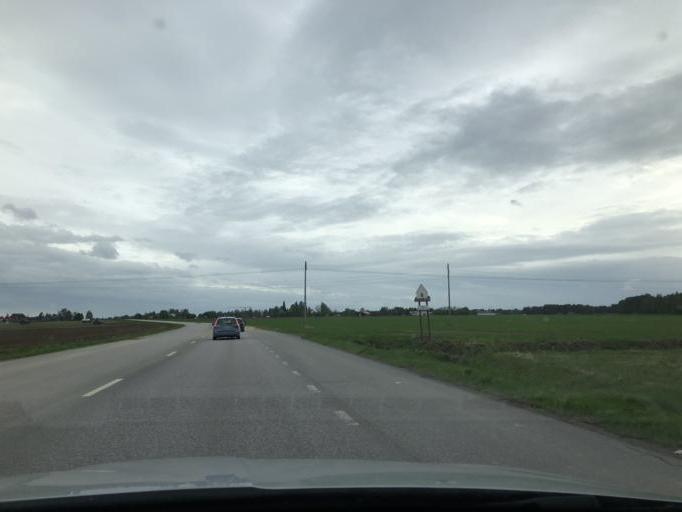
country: SE
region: Norrbotten
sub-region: Pitea Kommun
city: Bergsviken
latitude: 65.3632
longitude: 21.4066
